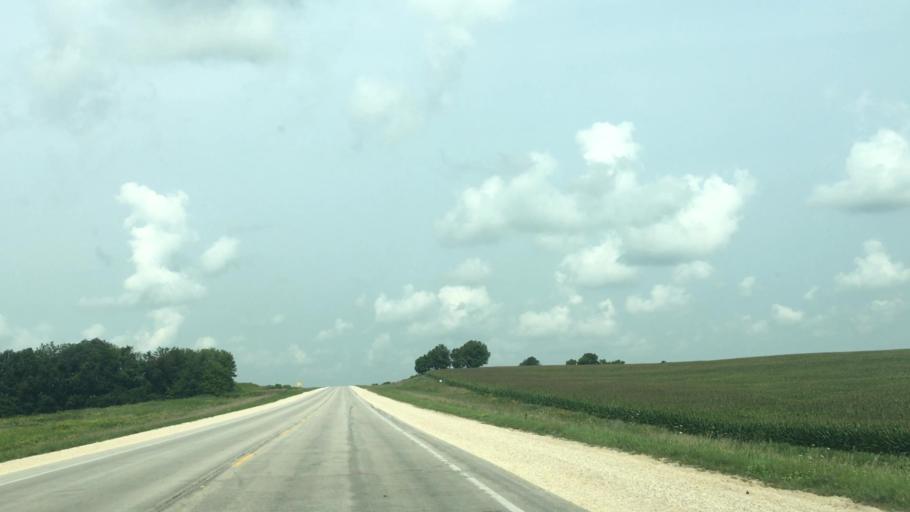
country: US
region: Iowa
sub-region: Winneshiek County
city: Decorah
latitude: 43.3782
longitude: -91.8174
